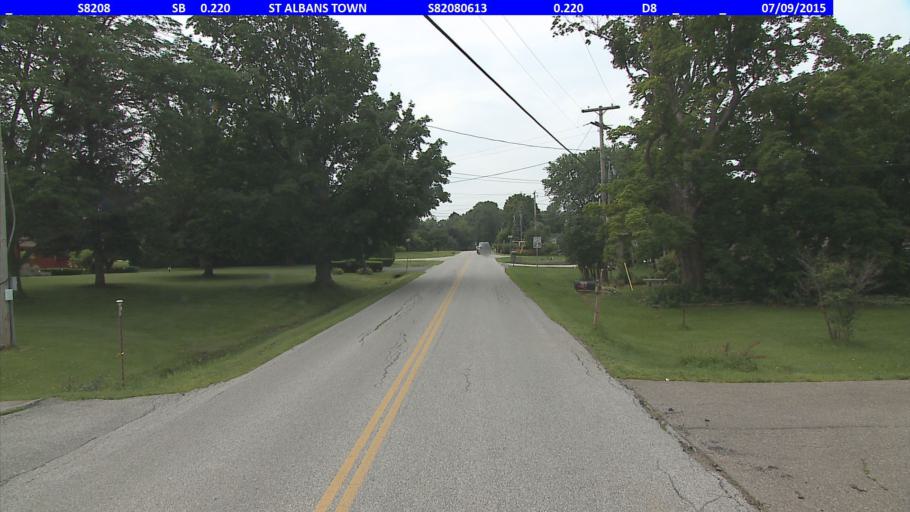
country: US
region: Vermont
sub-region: Franklin County
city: Saint Albans
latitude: 44.8270
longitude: -73.0756
